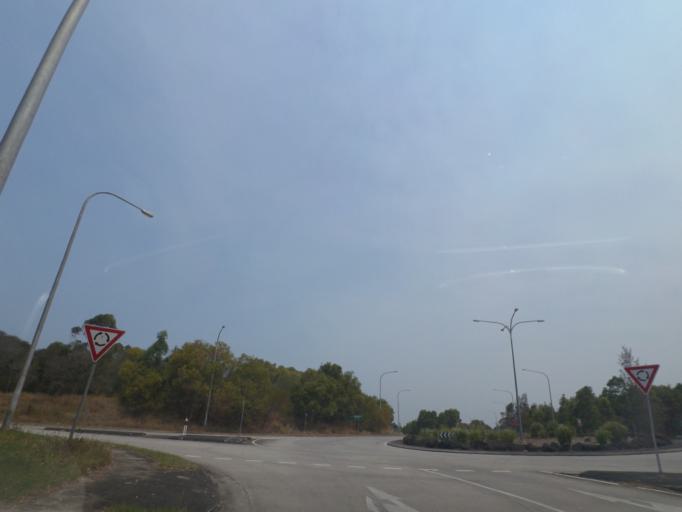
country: AU
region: New South Wales
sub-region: Byron Shire
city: Brunswick Heads
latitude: -28.4914
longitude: 153.5209
